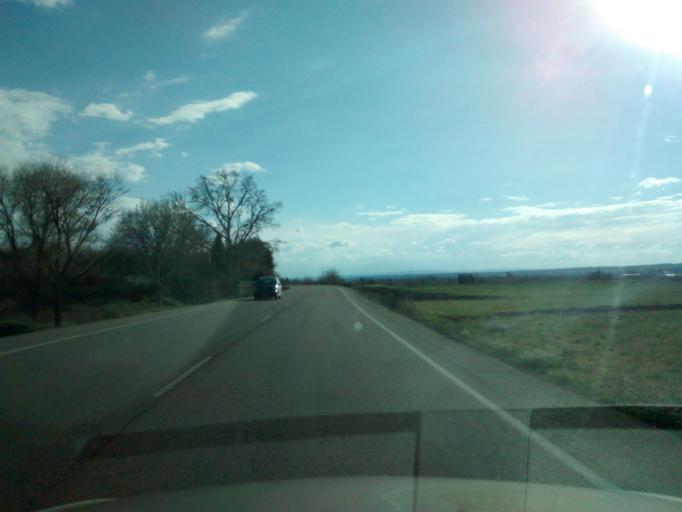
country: ES
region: Aragon
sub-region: Provincia de Zaragoza
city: Villanueva de Gallego
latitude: 41.7730
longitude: -0.7907
